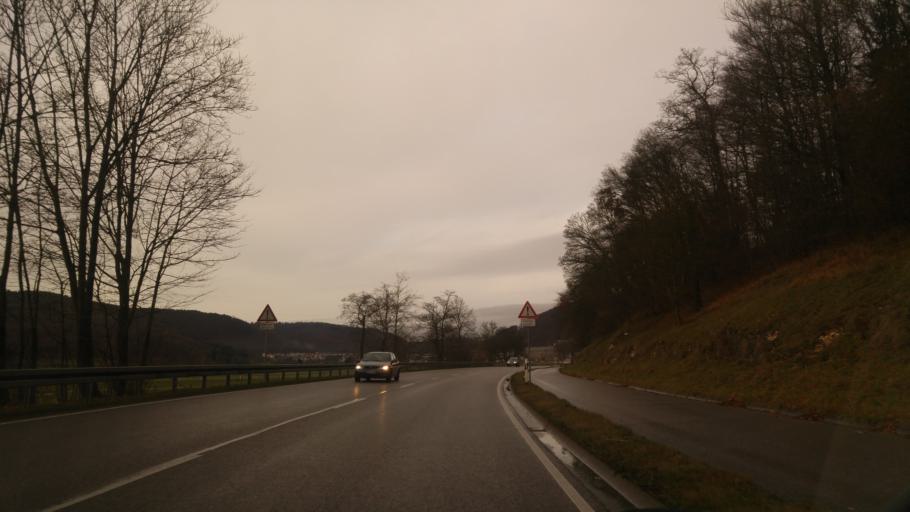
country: DE
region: Baden-Wuerttemberg
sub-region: Regierungsbezirk Stuttgart
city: Konigsbronn
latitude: 48.7559
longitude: 10.1027
